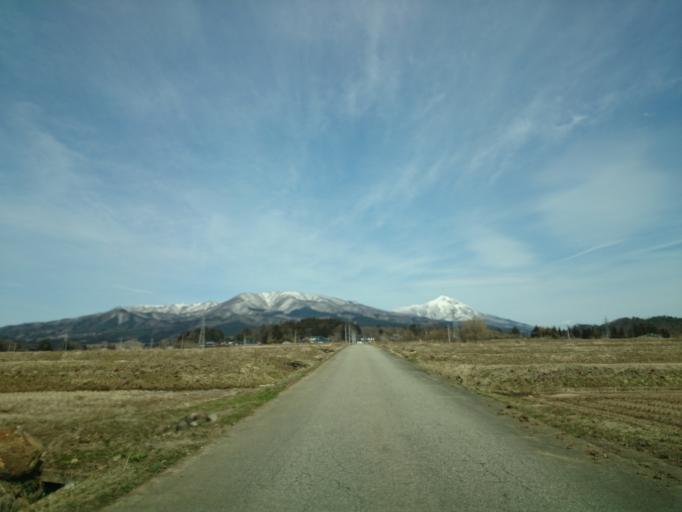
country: JP
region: Fukushima
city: Kitakata
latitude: 37.5586
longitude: 139.9268
